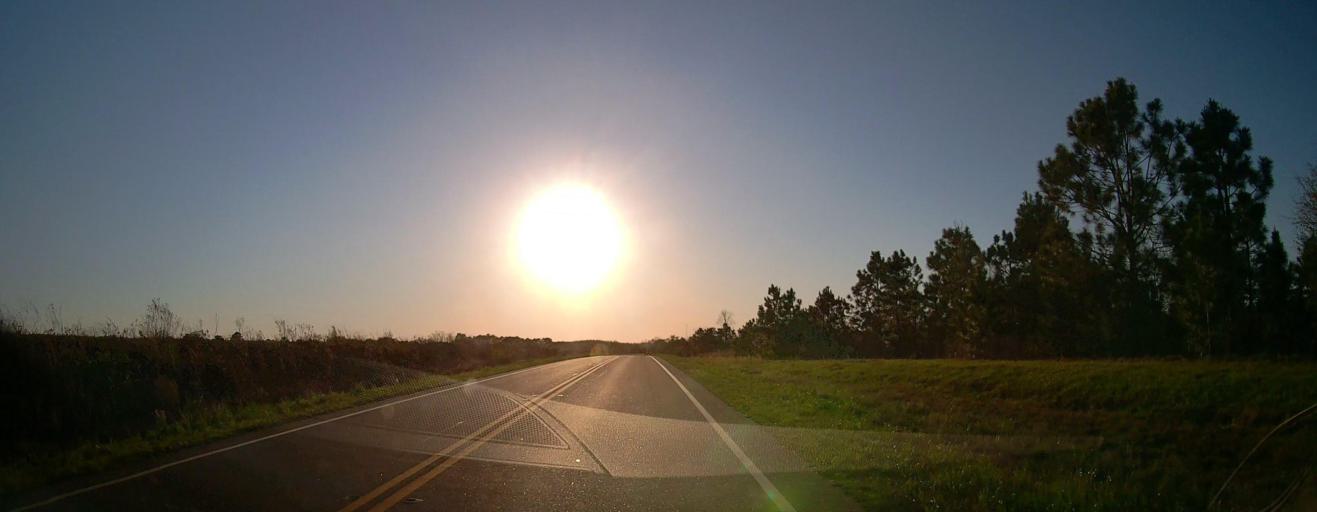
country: US
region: Georgia
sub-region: Wilcox County
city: Rochelle
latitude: 31.9491
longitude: -83.4977
